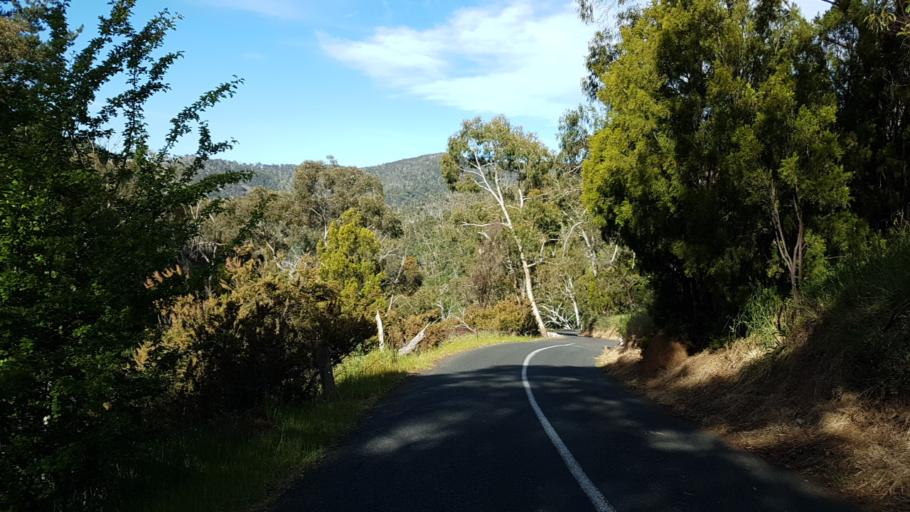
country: AU
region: South Australia
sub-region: Adelaide Hills
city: Adelaide Hills
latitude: -34.9101
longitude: 138.7697
